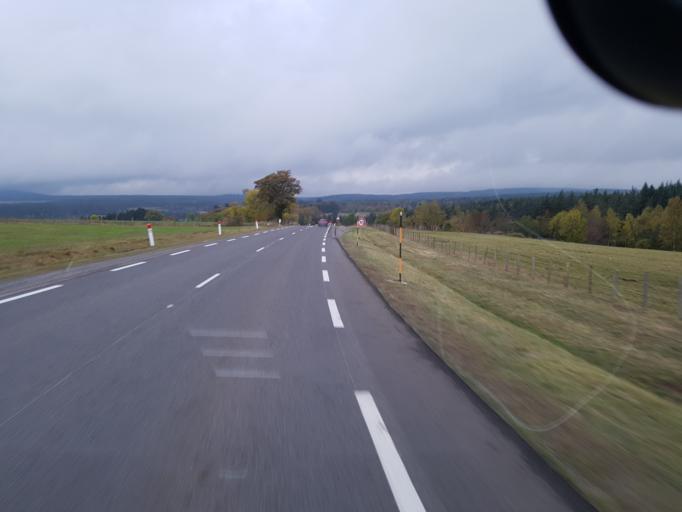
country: FR
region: Languedoc-Roussillon
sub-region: Departement de la Lozere
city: Mende
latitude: 44.5841
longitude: 3.6505
